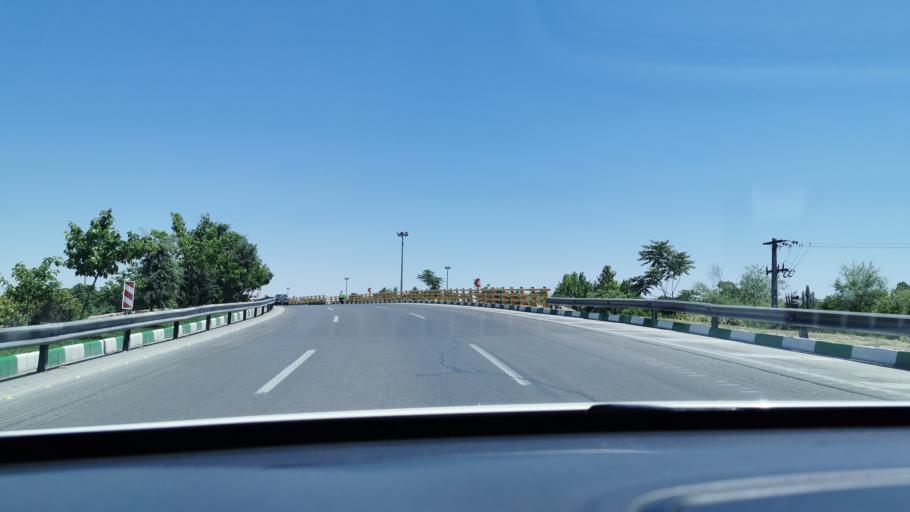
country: IR
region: Razavi Khorasan
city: Mashhad
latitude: 36.2499
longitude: 59.6080
